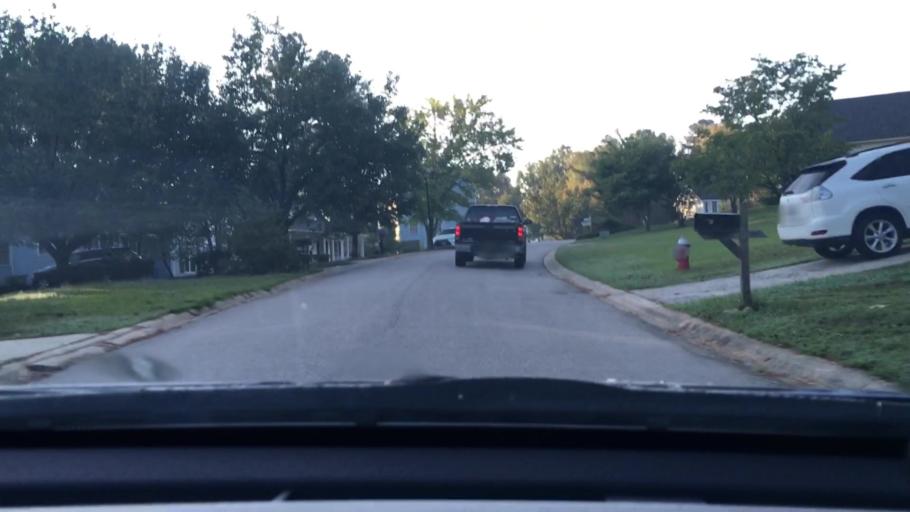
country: US
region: South Carolina
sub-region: Lexington County
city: Irmo
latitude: 34.1023
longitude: -81.1550
